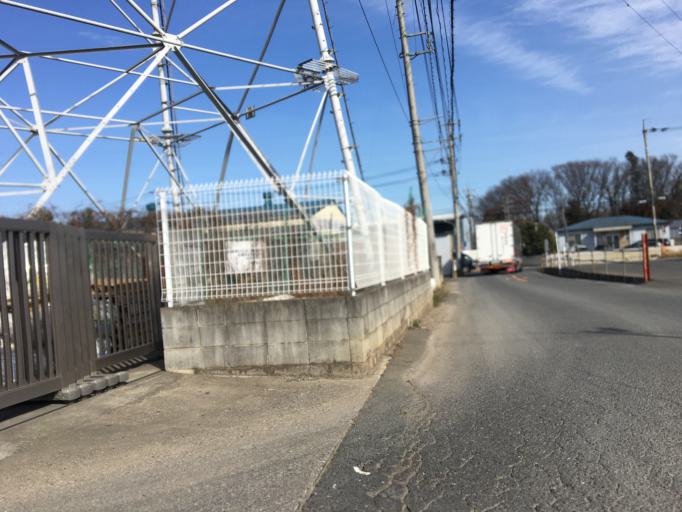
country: JP
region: Saitama
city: Oi
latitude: 35.8221
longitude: 139.5246
